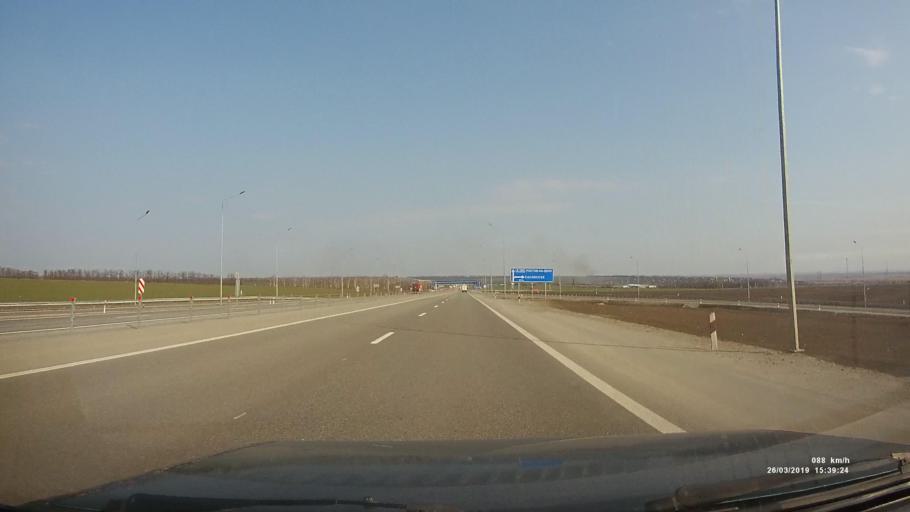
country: RU
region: Rostov
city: Sinyavskoye
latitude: 47.2941
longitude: 39.2842
